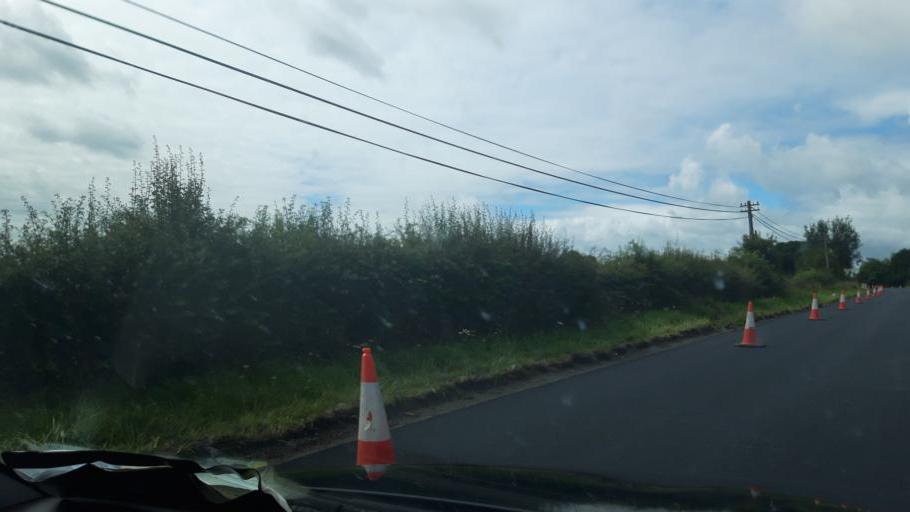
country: IE
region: Leinster
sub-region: Kilkenny
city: Callan
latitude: 52.5635
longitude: -7.3604
